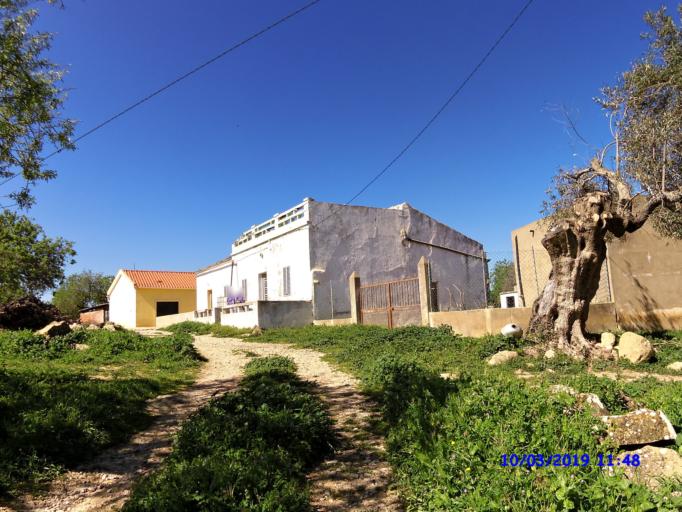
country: PT
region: Faro
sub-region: Loule
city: Boliqueime
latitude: 37.1650
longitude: -8.1387
